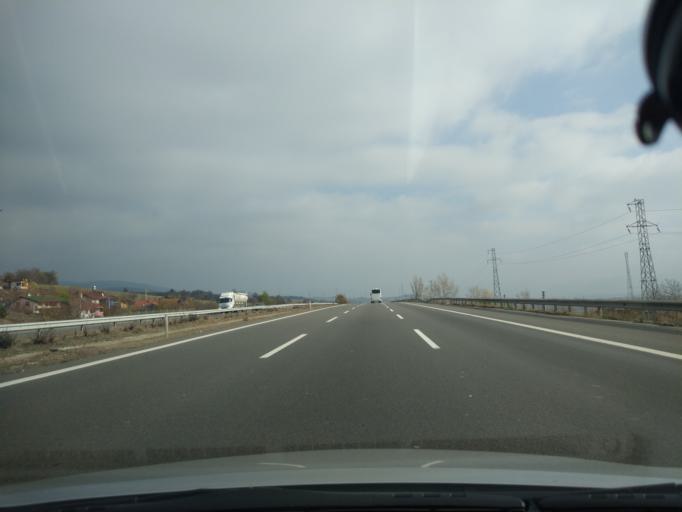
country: TR
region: Bolu
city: Bolu
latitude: 40.7636
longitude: 31.6123
